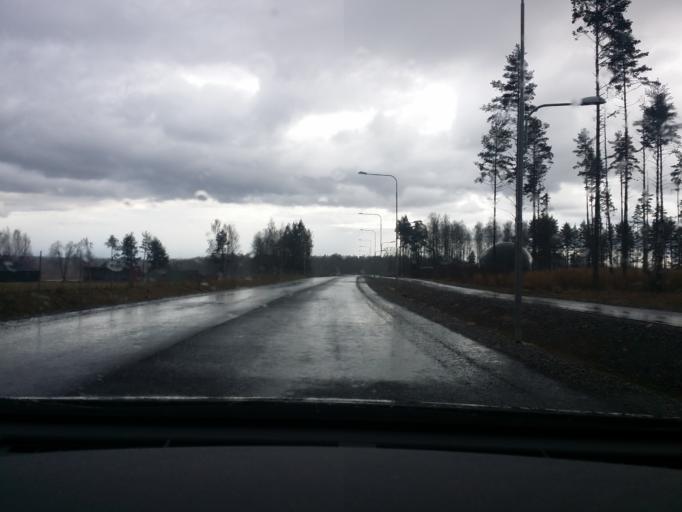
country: SE
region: Soedermanland
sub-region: Eskilstuna Kommun
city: Arla
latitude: 59.3460
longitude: 16.7018
